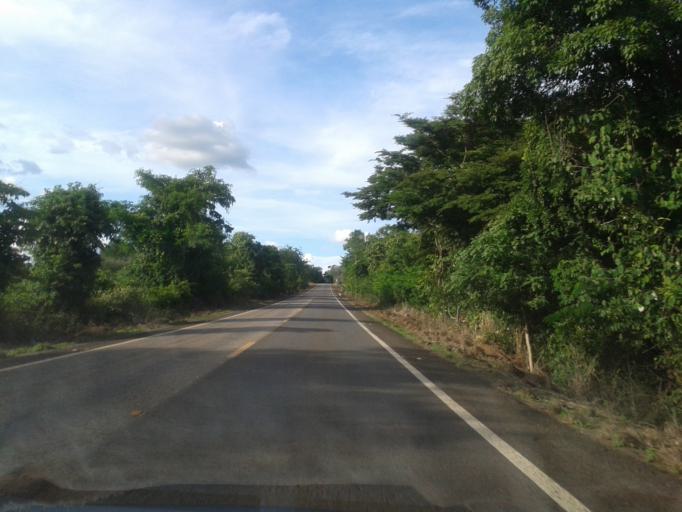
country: BR
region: Goias
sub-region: Crixas
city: Crixas
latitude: -13.9817
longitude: -50.3226
